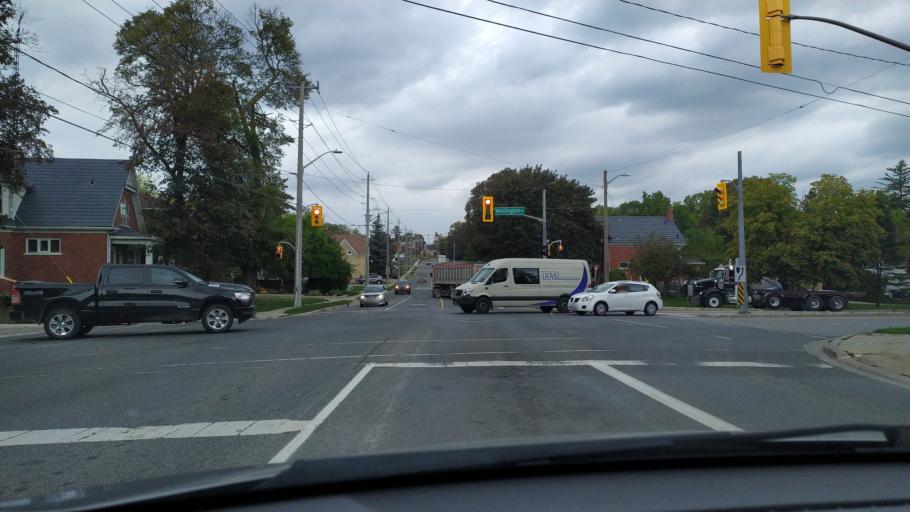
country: CA
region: Ontario
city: Waterloo
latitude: 43.4608
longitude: -80.4833
